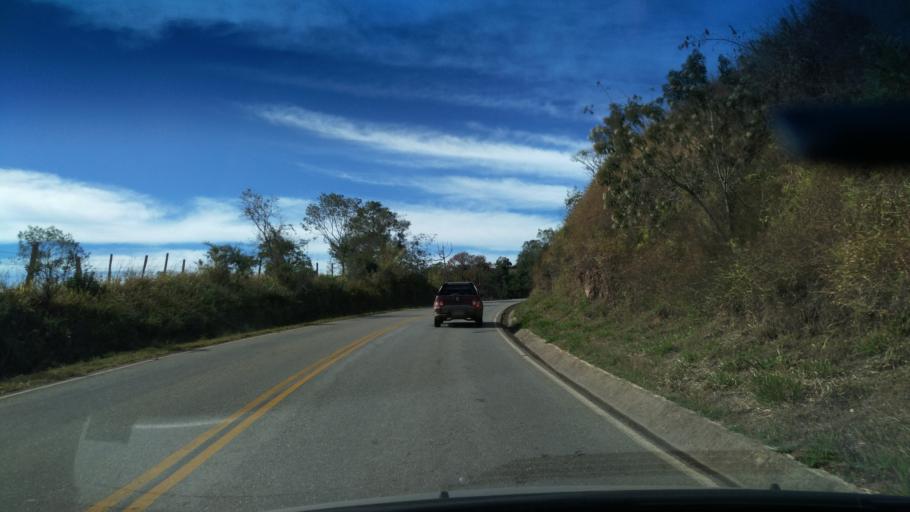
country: BR
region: Minas Gerais
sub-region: Andradas
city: Andradas
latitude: -22.0677
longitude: -46.4561
